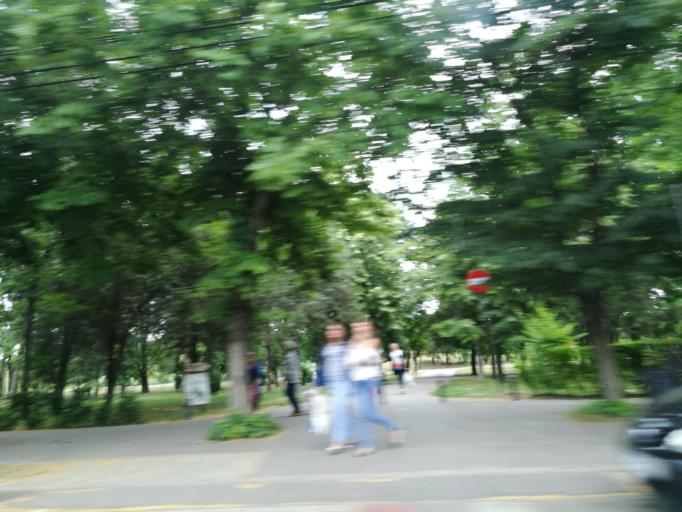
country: RO
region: Constanta
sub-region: Municipiul Constanta
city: Constanta
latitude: 44.2064
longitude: 28.6294
